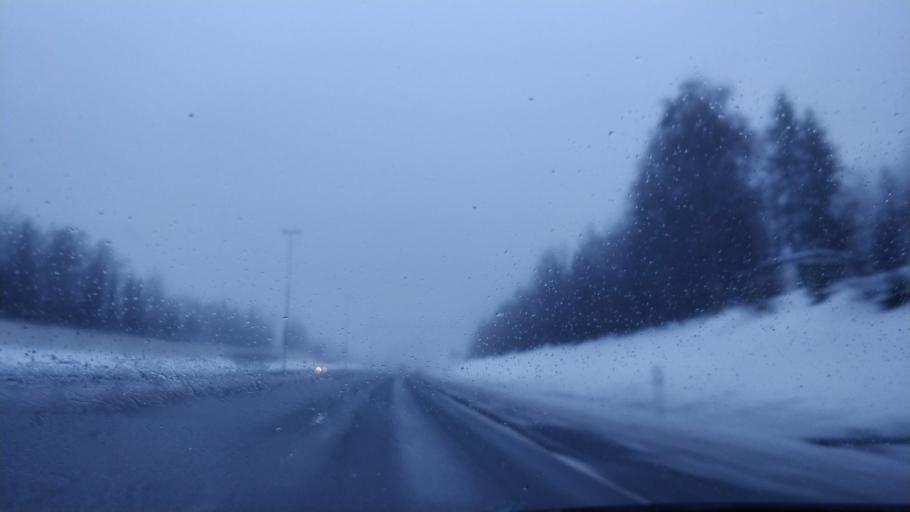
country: FI
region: Lapland
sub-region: Kemi-Tornio
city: Kemi
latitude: 65.7509
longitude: 24.5754
